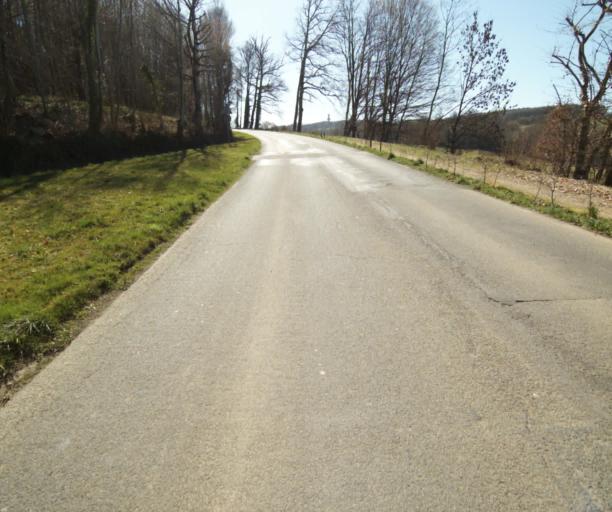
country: FR
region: Limousin
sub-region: Departement de la Correze
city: Seilhac
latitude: 45.3672
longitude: 1.7060
